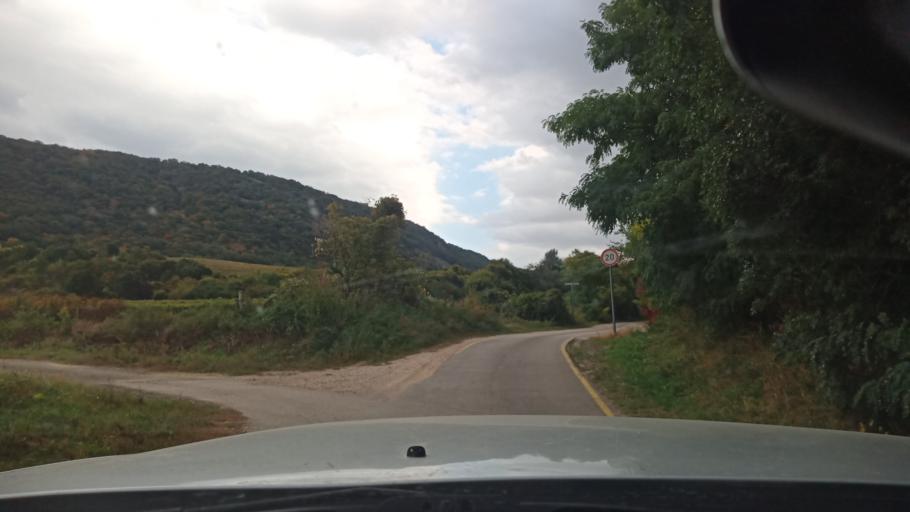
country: HU
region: Fejer
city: Mor
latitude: 47.3728
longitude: 18.2381
